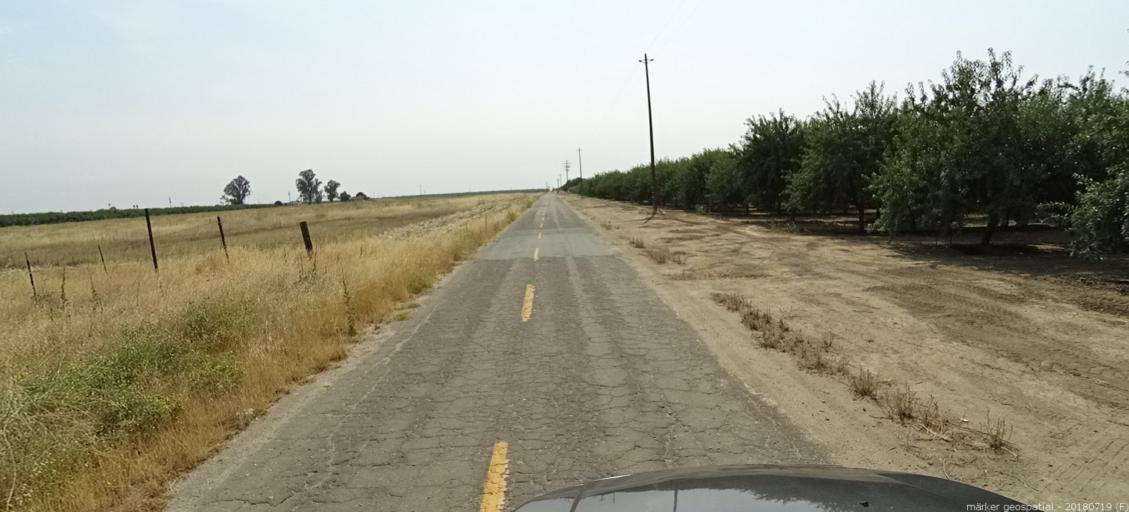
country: US
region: California
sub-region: Madera County
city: Fairmead
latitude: 37.0837
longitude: -120.1888
